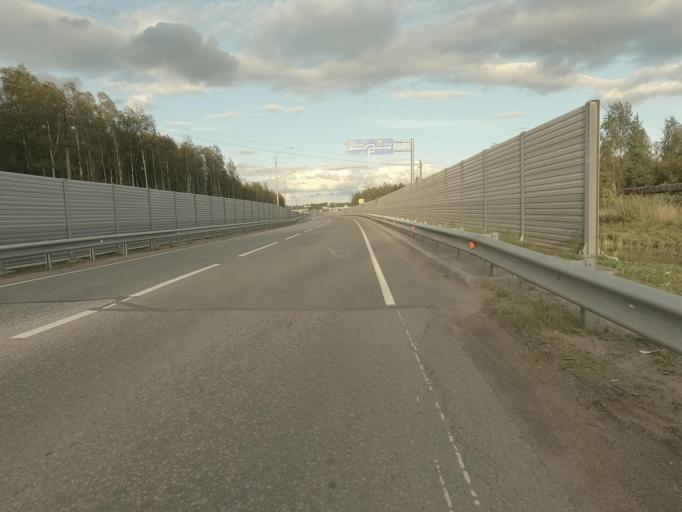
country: RU
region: Leningrad
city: Mga
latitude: 59.7572
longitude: 31.0811
